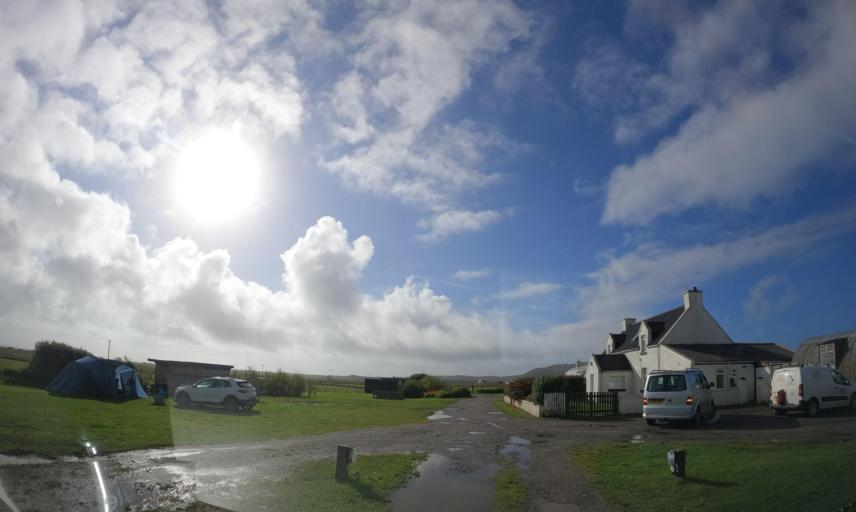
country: GB
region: Scotland
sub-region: Eilean Siar
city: Barra
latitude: 56.4777
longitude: -6.9216
